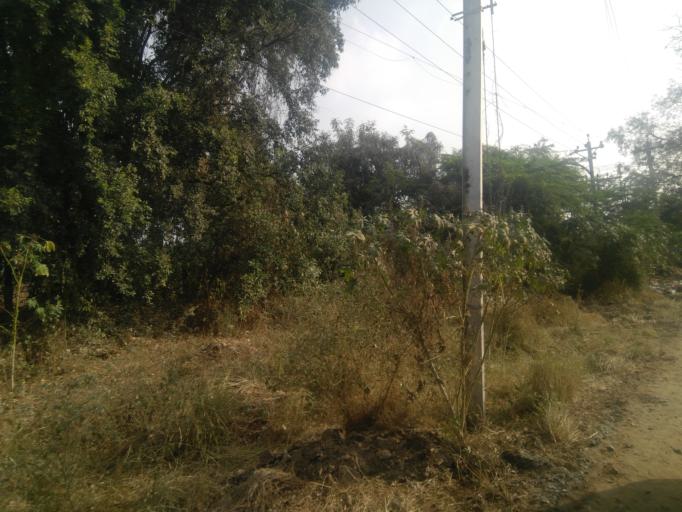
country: IN
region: Tamil Nadu
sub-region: Coimbatore
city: Periyanayakkanpalaiyam
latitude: 11.0794
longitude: 76.9380
